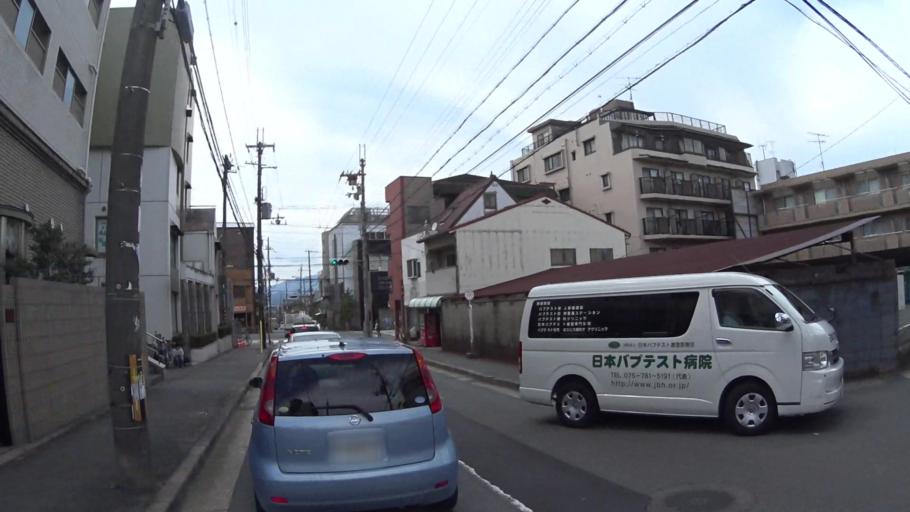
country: JP
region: Kyoto
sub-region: Kyoto-shi
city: Kamigyo-ku
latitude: 35.0328
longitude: 135.7917
